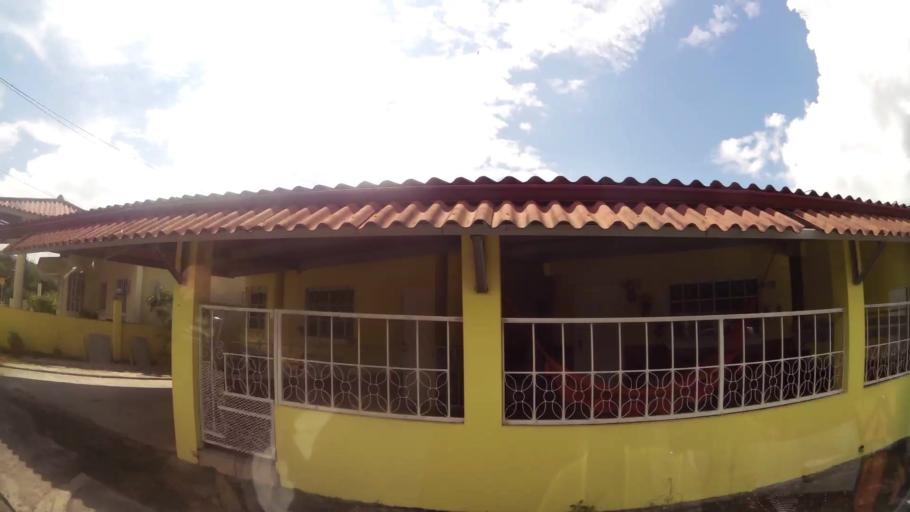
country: PA
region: Panama
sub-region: Distrito Arraijan
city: Arraijan
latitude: 8.9460
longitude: -79.6761
